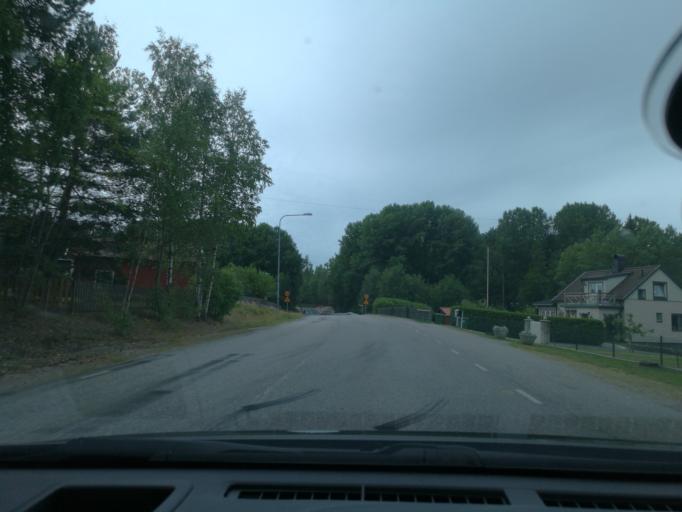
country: SE
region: Vaestmanland
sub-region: Kungsors Kommun
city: Kungsoer
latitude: 59.4067
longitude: 16.1077
